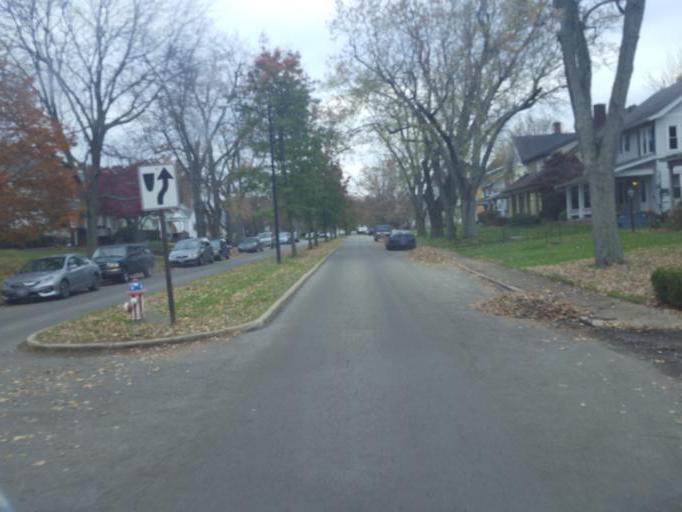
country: US
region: Ohio
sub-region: Richland County
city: Mansfield
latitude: 40.7574
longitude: -82.5379
